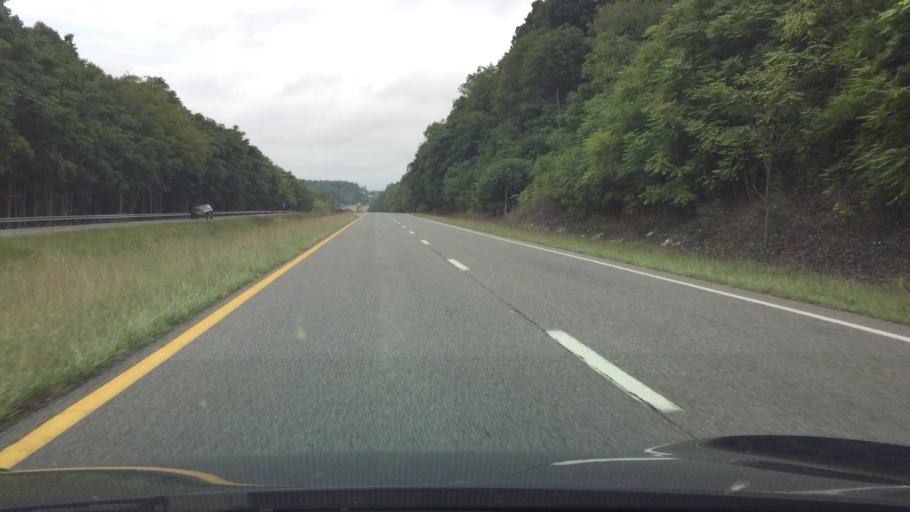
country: US
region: Virginia
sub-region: City of Radford
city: Radford
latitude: 37.1106
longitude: -80.5230
